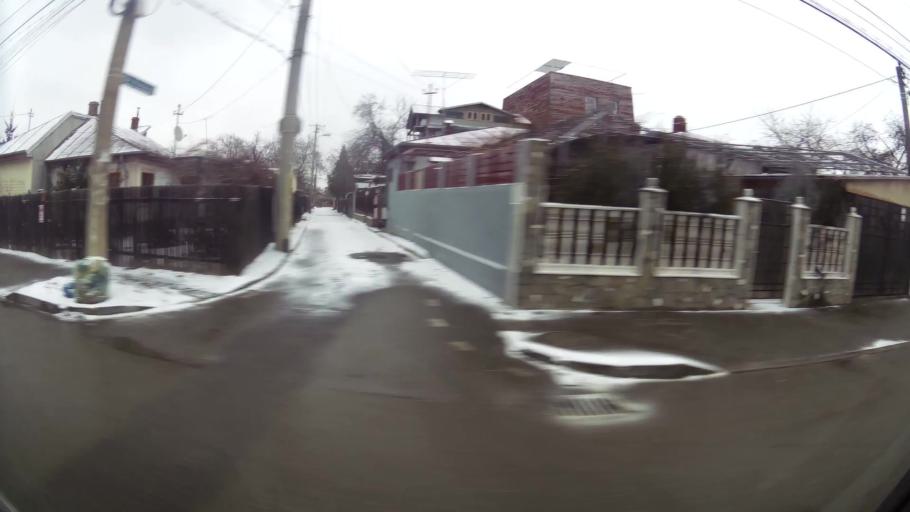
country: RO
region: Prahova
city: Ploiesti
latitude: 44.9317
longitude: 26.0430
